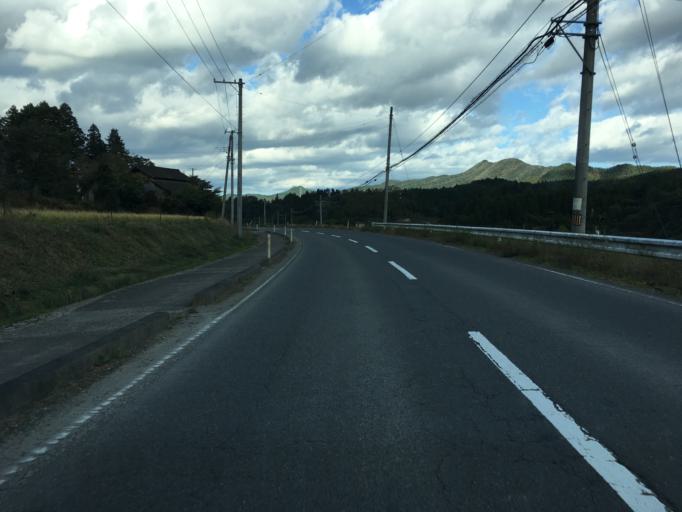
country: JP
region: Miyagi
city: Marumori
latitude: 37.8415
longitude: 140.8300
